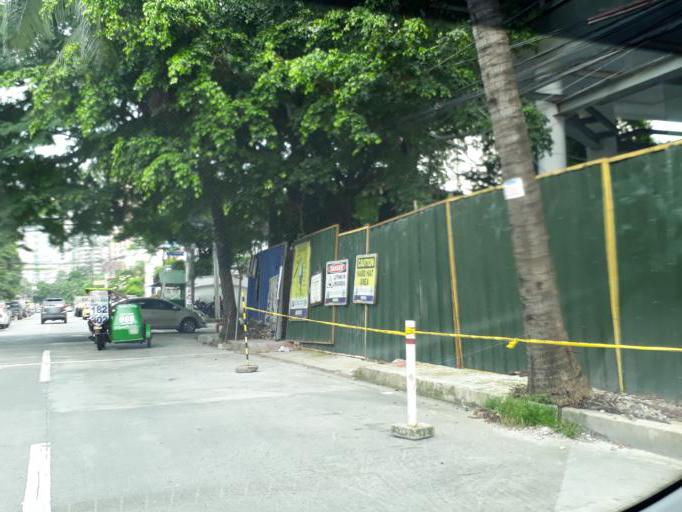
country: PH
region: Calabarzon
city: Del Monte
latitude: 14.6343
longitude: 121.0335
